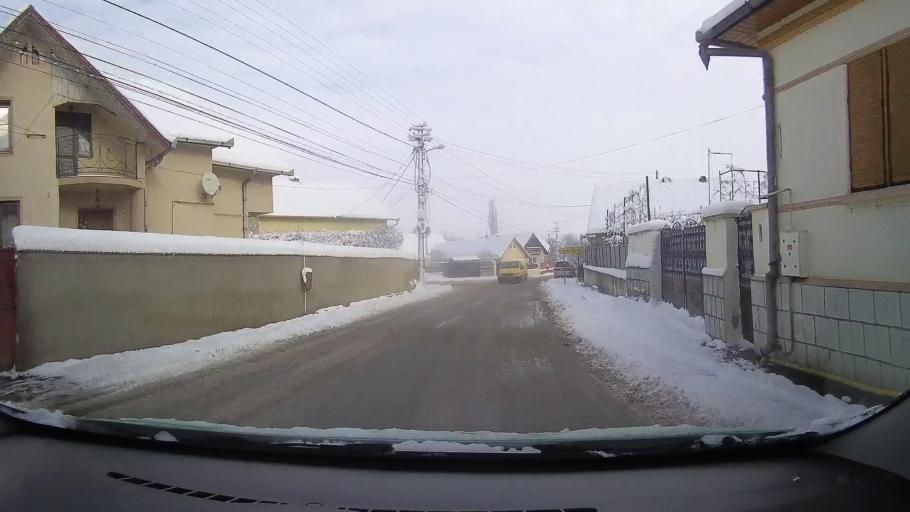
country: RO
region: Alba
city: Vurpar
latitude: 45.9780
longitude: 23.4816
